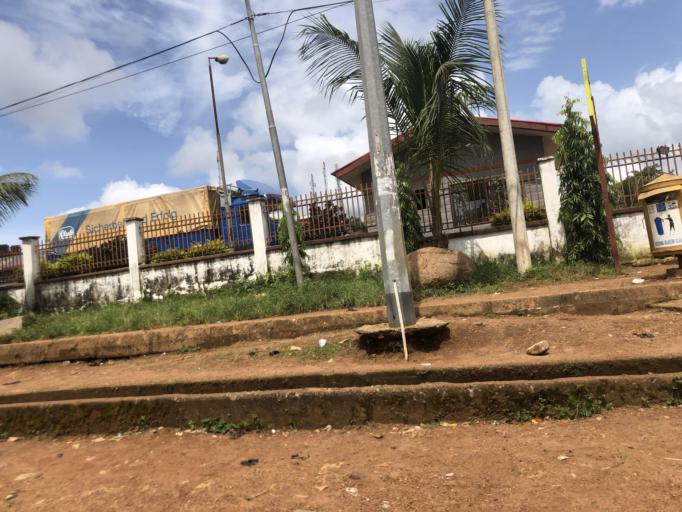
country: SL
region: Northern Province
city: Makeni
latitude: 8.8750
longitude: -12.0510
